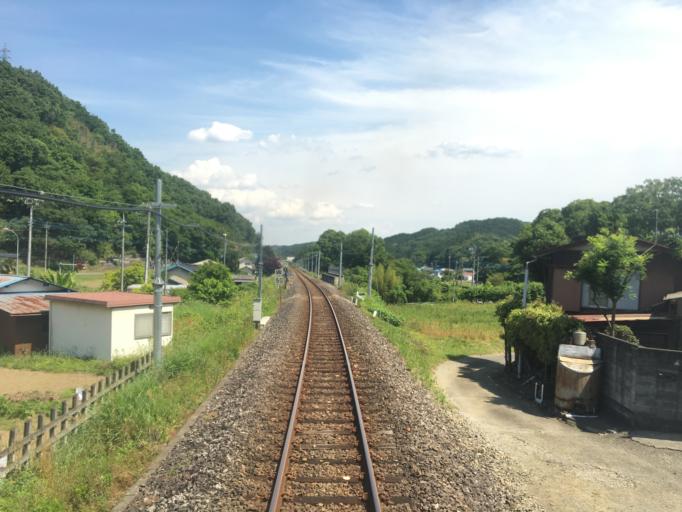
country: JP
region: Saitama
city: Yorii
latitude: 36.0801
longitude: 139.2195
